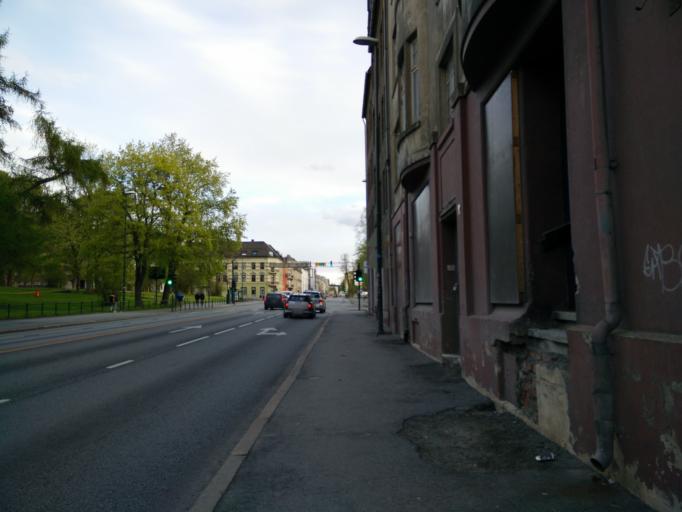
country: NO
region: Sor-Trondelag
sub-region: Trondheim
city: Trondheim
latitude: 63.4218
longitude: 10.3947
